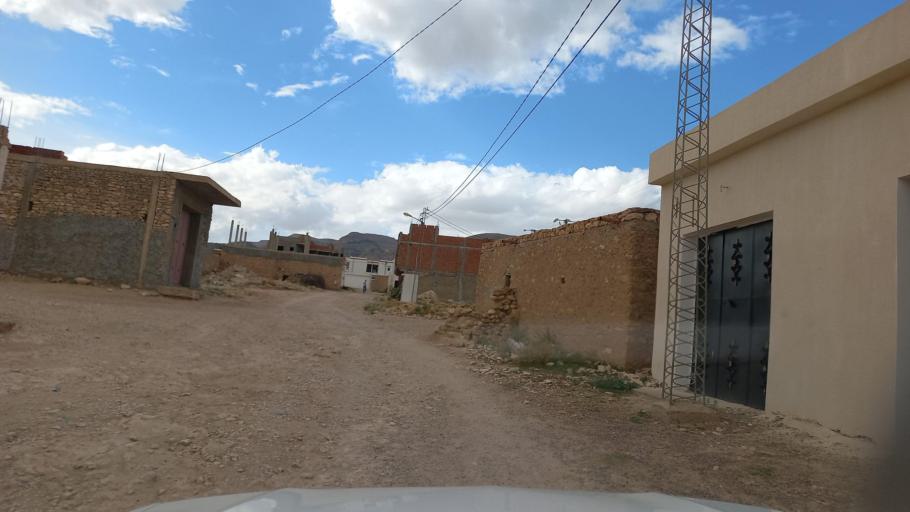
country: TN
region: Al Qasrayn
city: Sbiba
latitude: 35.4464
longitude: 9.0791
